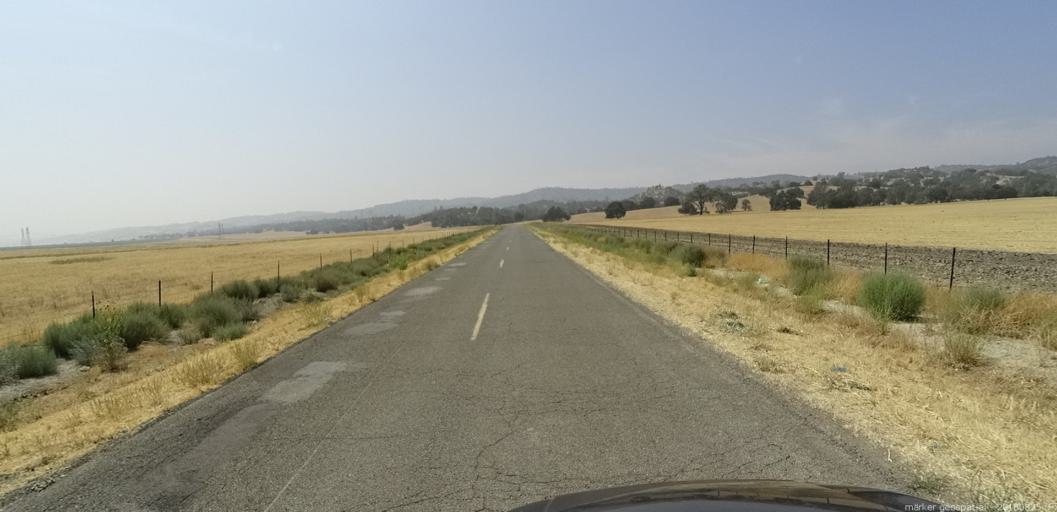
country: US
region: California
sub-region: San Luis Obispo County
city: Shandon
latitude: 35.8297
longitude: -120.3840
